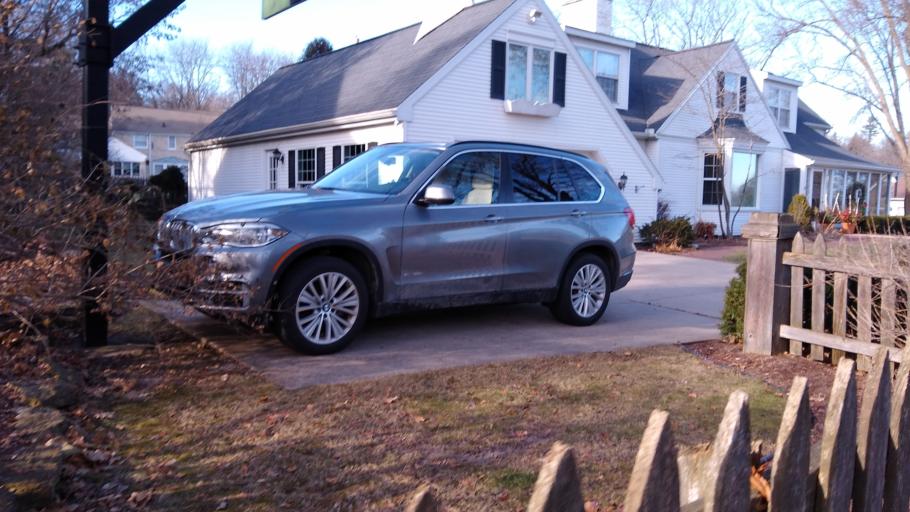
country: US
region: Wisconsin
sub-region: Dane County
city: Shorewood Hills
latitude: 43.0432
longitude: -89.4409
